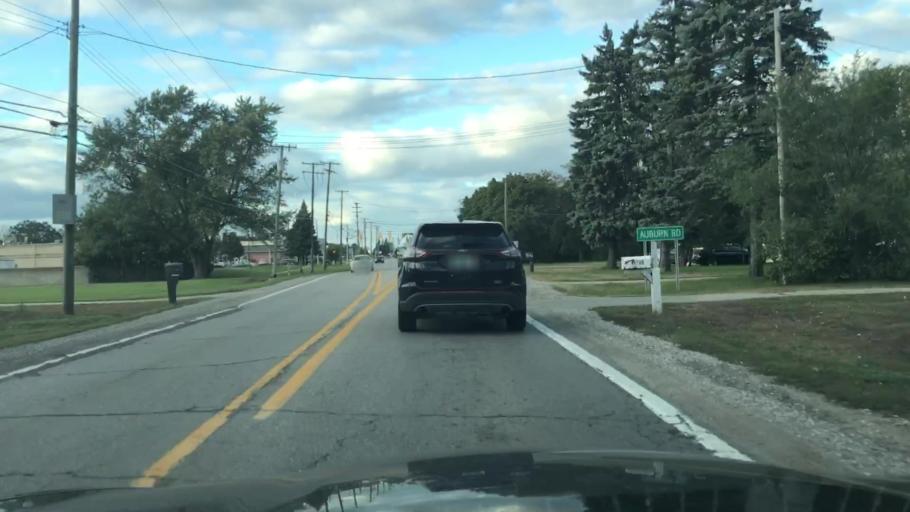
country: US
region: Michigan
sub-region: Macomb County
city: Utica
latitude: 42.6375
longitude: -83.0725
